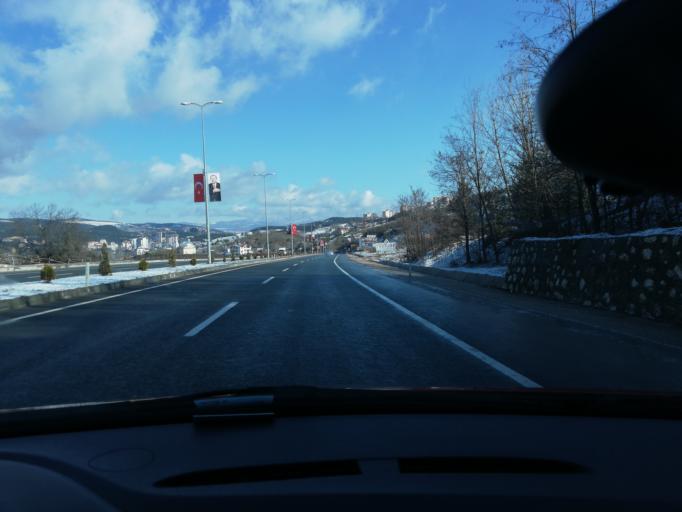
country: TR
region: Kastamonu
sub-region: Cide
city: Kastamonu
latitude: 41.3402
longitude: 33.7656
